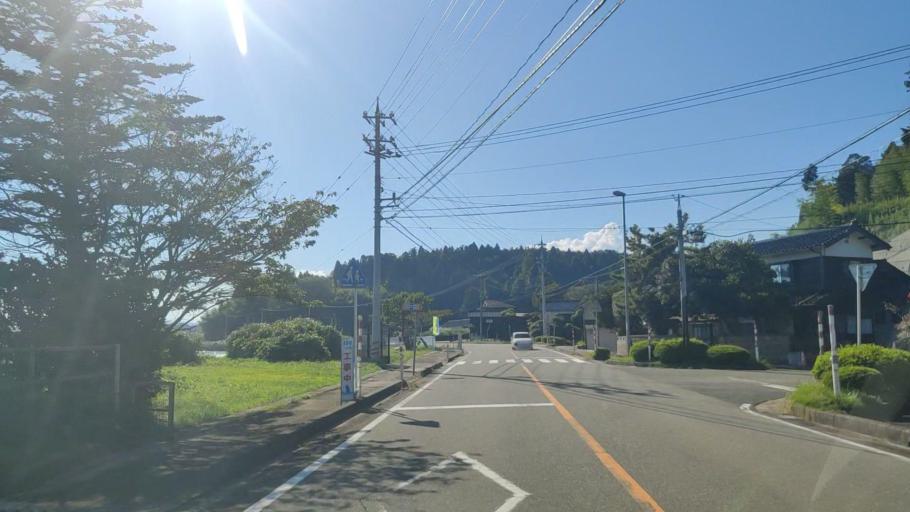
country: JP
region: Ishikawa
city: Nanao
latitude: 37.2367
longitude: 136.9614
